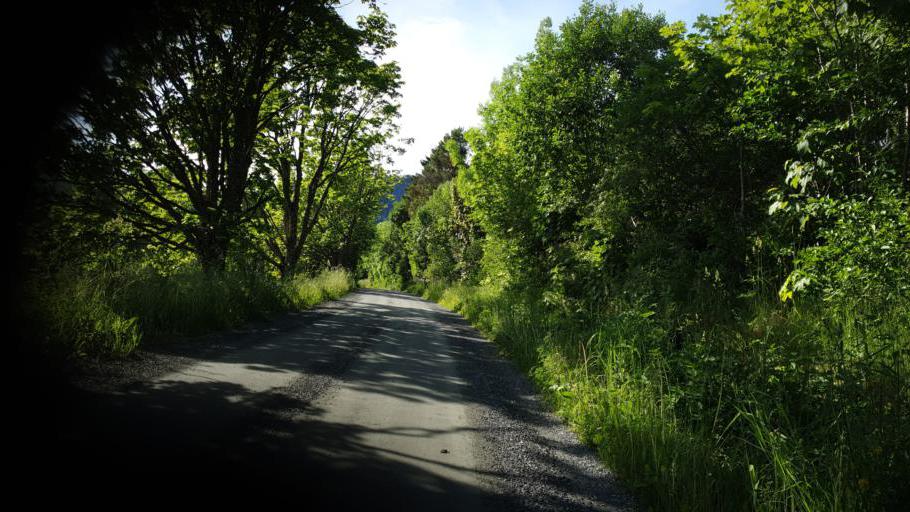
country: NO
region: Sor-Trondelag
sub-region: Trondheim
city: Trondheim
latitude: 63.5745
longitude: 10.3945
